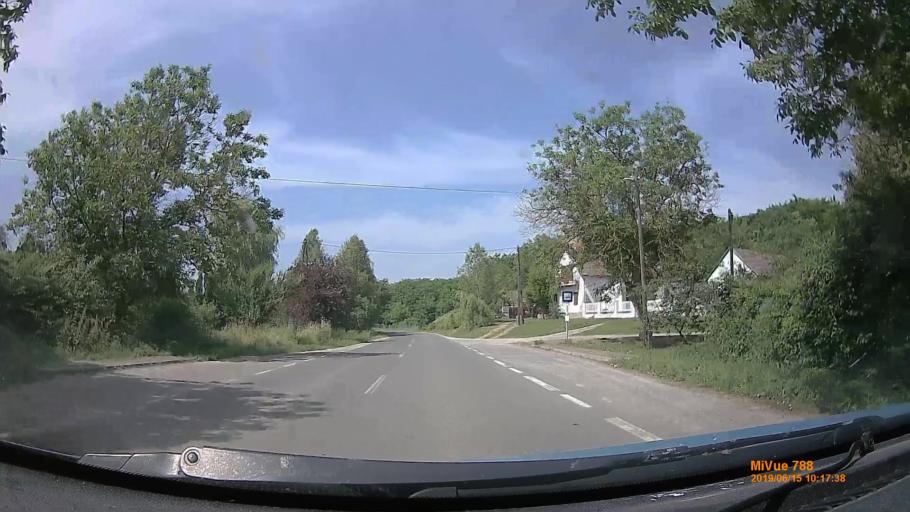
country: HU
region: Baranya
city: Buekkoesd
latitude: 46.1247
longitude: 18.0036
